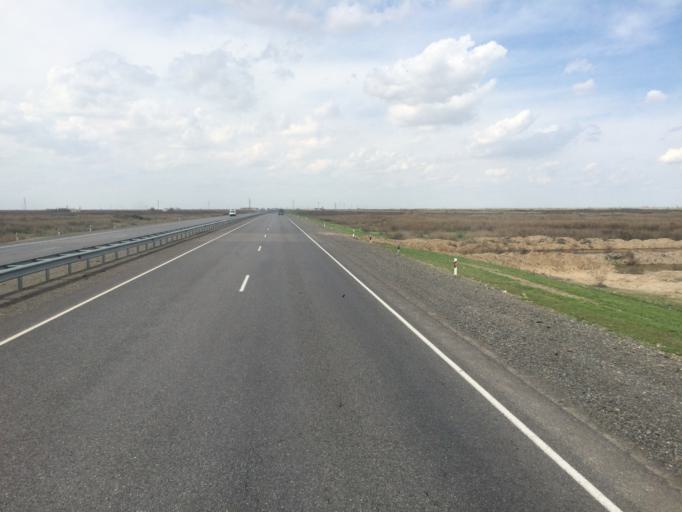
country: KZ
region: Qyzylorda
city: Zhangaqorghan
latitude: 43.9951
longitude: 67.2270
